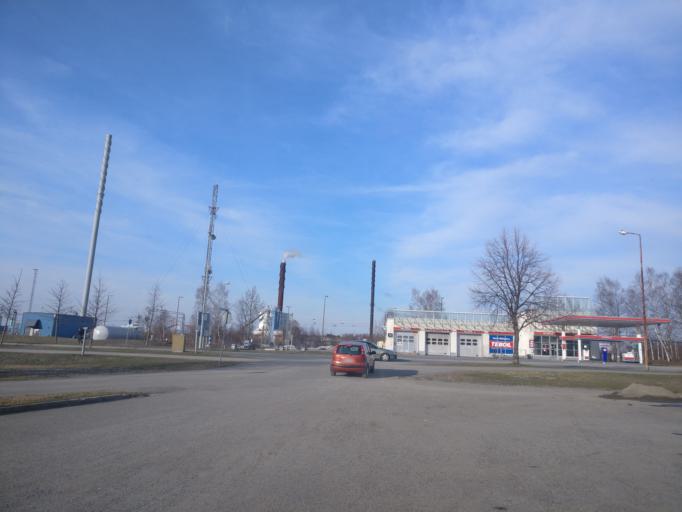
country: FI
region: Lapland
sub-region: Kemi-Tornio
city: Kemi
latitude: 65.7310
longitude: 24.5777
